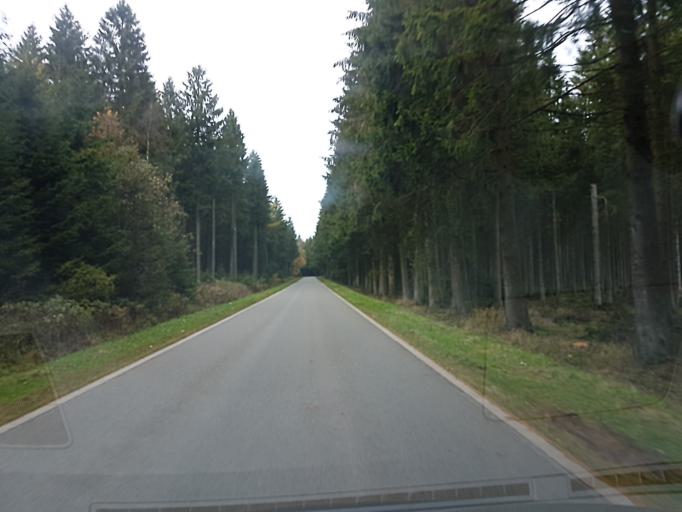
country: BE
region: Wallonia
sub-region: Province de Liege
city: Malmedy
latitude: 50.4723
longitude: 6.0269
